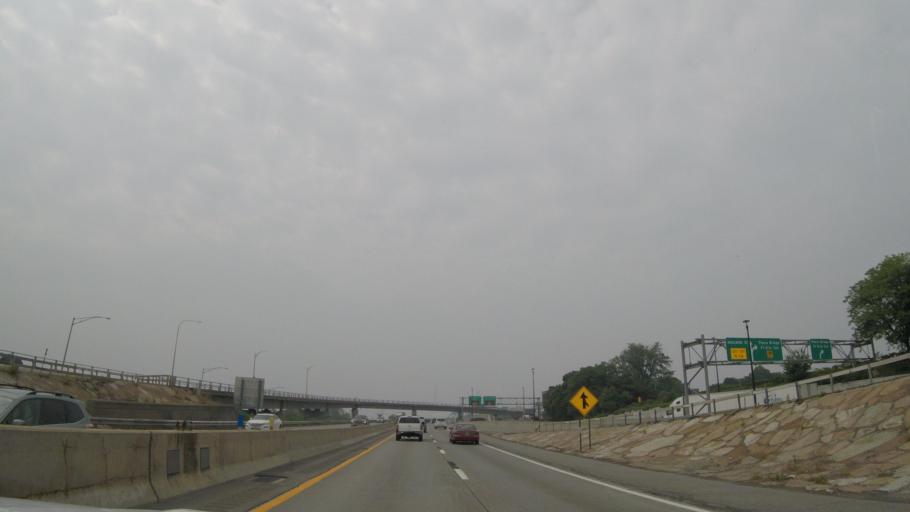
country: US
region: New York
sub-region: Erie County
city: Buffalo
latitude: 42.8997
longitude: -78.8990
